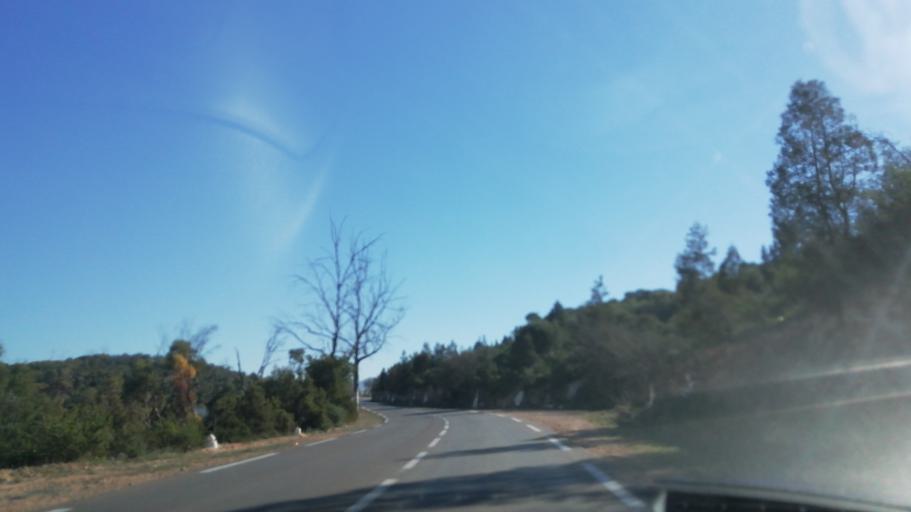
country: DZ
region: Tlemcen
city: Beni Mester
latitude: 34.8171
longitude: -1.6349
